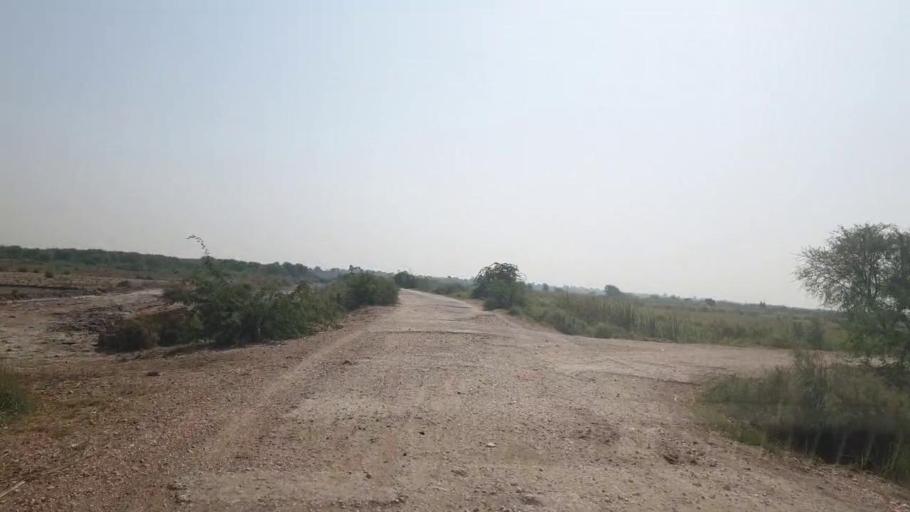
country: PK
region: Sindh
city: Berani
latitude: 25.8897
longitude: 68.7530
